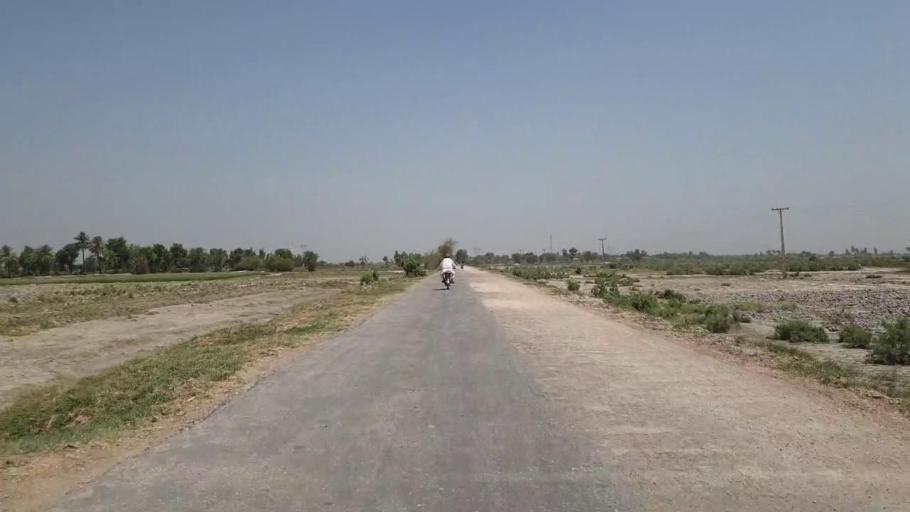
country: PK
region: Sindh
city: Adilpur
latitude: 27.8821
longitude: 69.2872
